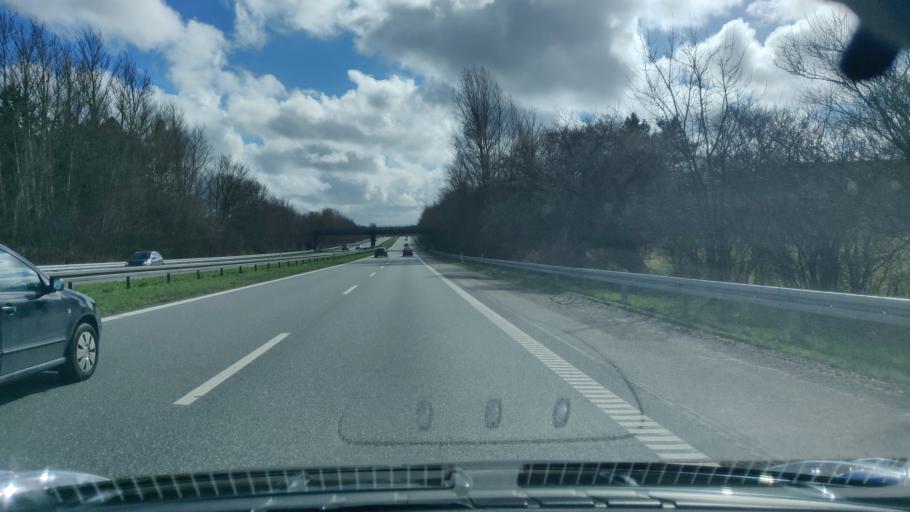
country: DK
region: Zealand
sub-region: Holbaek Kommune
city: Vipperod
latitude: 55.6640
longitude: 11.7594
